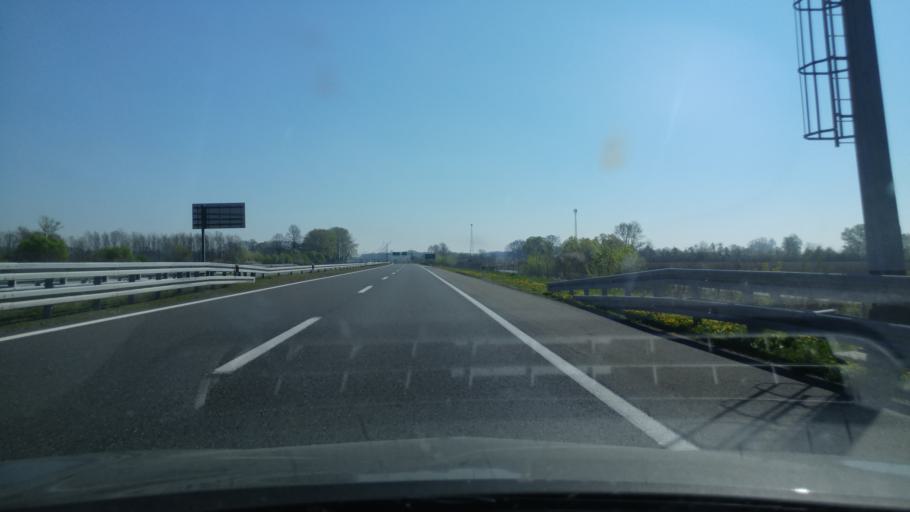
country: HR
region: Brodsko-Posavska
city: Garcin
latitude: 45.1454
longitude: 18.2933
